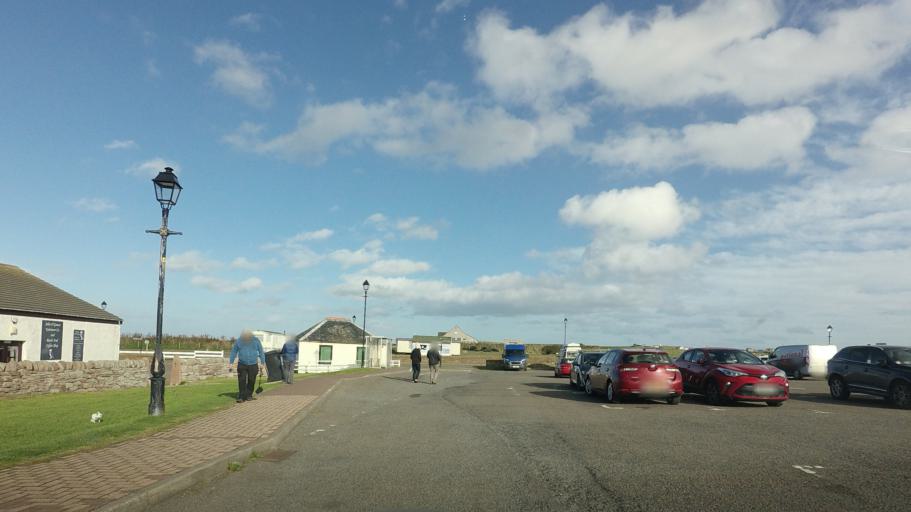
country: GB
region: Scotland
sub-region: Highland
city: Wick
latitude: 58.6433
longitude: -3.0695
